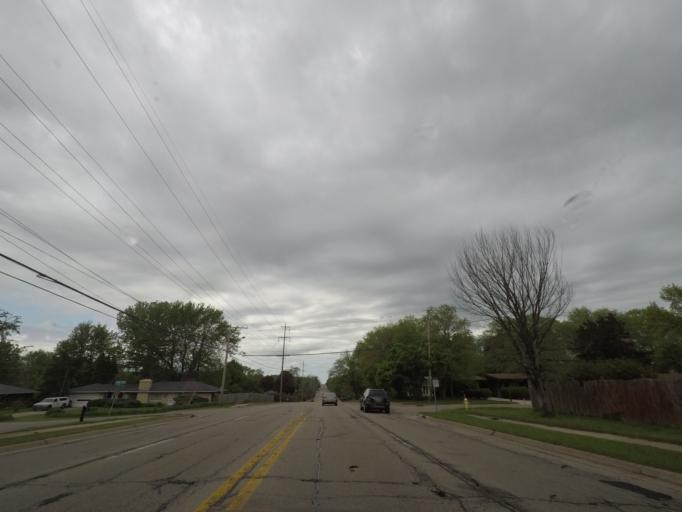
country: US
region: Illinois
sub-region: Winnebago County
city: Loves Park
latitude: 42.2911
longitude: -89.0291
